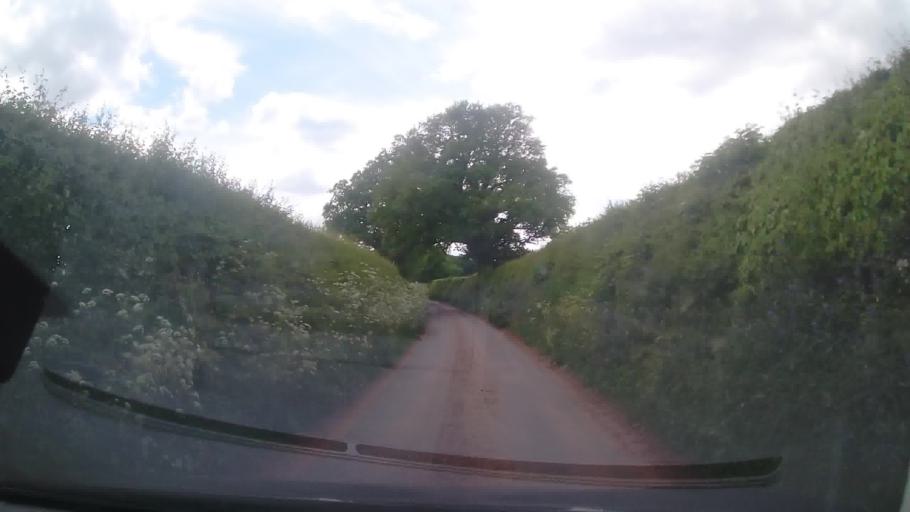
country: GB
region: England
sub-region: Shropshire
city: Clive
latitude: 52.8051
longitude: -2.7160
